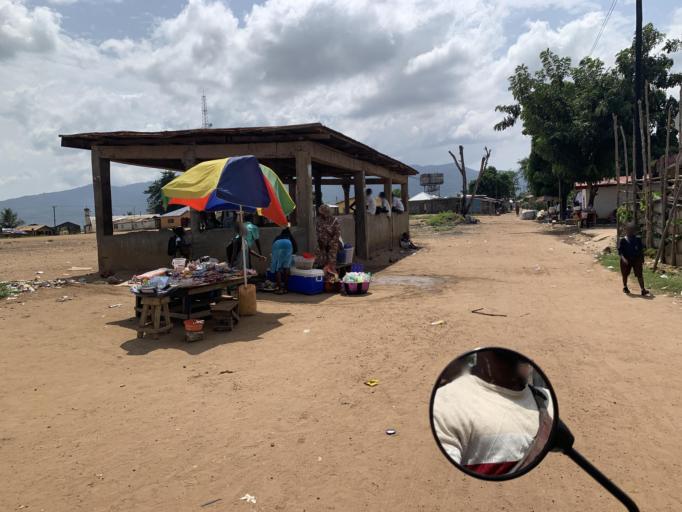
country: SL
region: Western Area
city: Hastings
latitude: 8.4102
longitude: -13.1322
